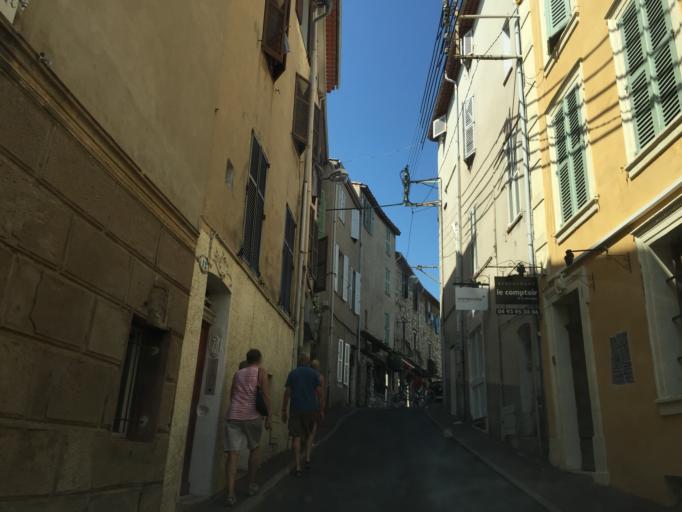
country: FR
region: Provence-Alpes-Cote d'Azur
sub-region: Departement des Alpes-Maritimes
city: Antibes
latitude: 43.5797
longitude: 7.1269
